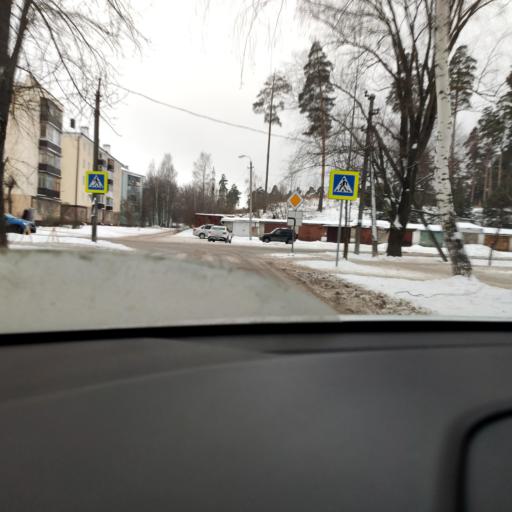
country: RU
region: Tatarstan
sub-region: Zelenodol'skiy Rayon
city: Zelenodolsk
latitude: 55.8534
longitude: 48.4838
